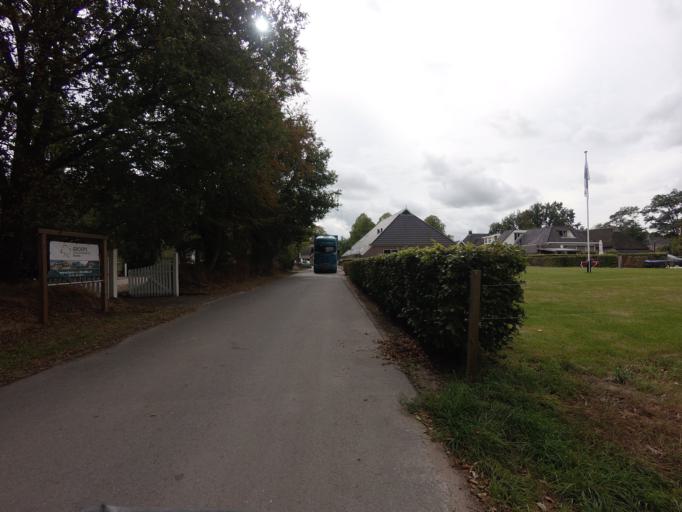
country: NL
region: Drenthe
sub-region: Gemeente Tynaarlo
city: Vries
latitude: 53.0681
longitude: 6.4651
